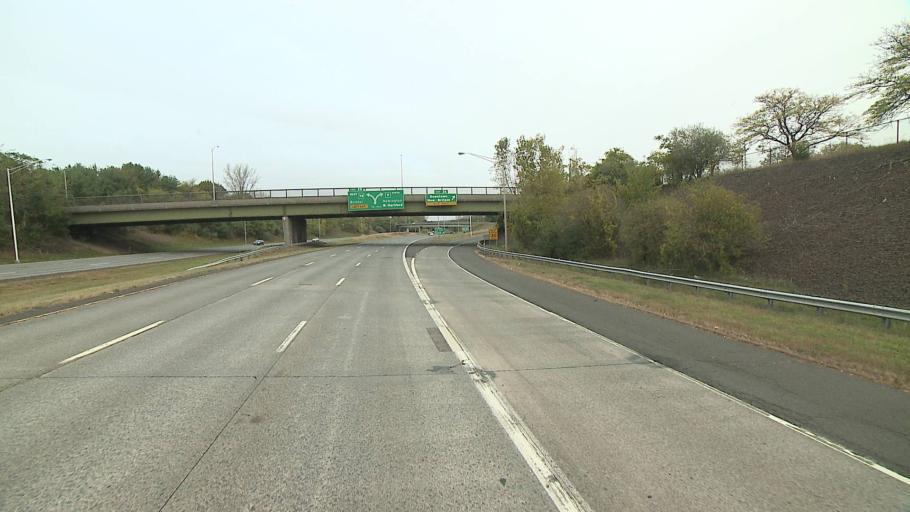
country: US
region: Connecticut
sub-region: Hartford County
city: New Britain
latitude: 41.6610
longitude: -72.7739
